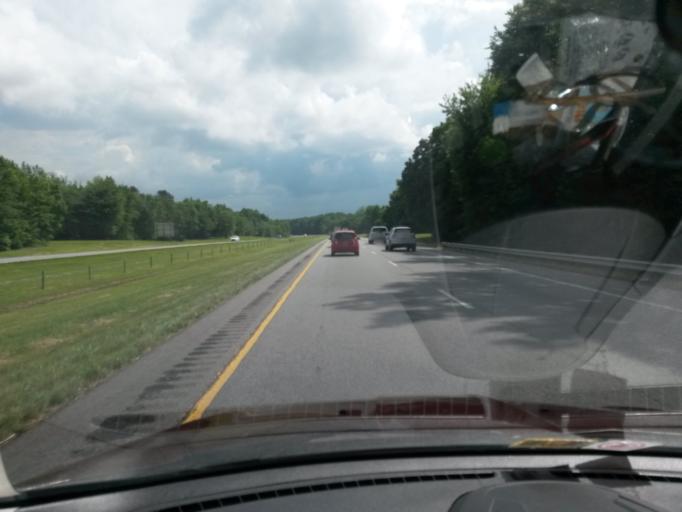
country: US
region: North Carolina
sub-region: Iredell County
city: Statesville
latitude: 35.9991
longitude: -80.8374
